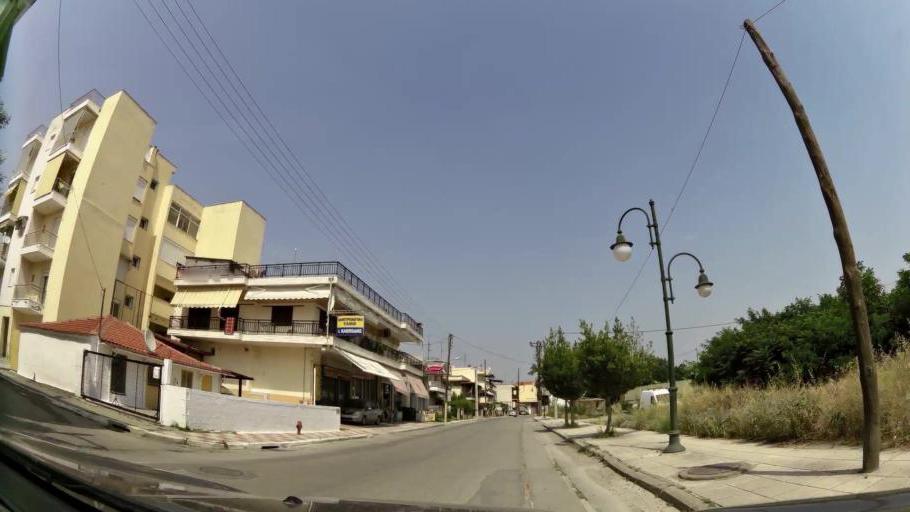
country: GR
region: Central Macedonia
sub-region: Nomos Thessalonikis
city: Nea Magnisia
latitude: 40.6863
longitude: 22.8498
